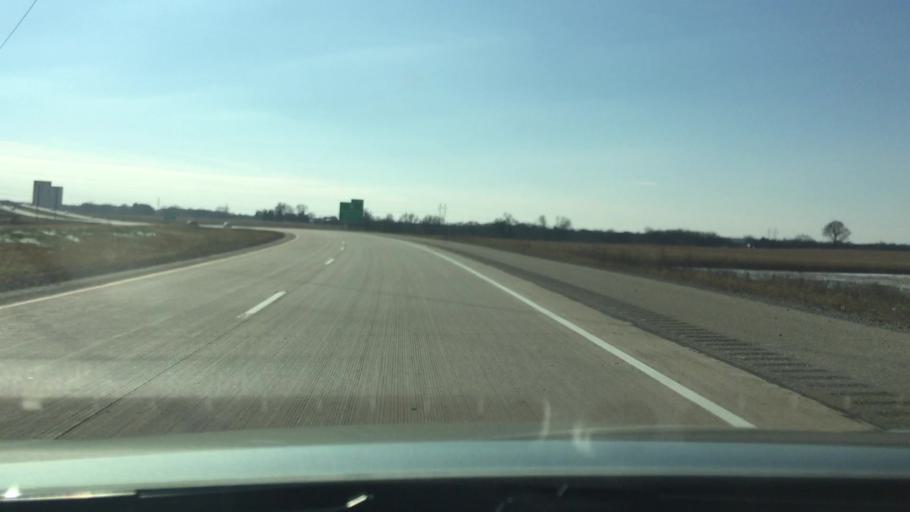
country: US
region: Wisconsin
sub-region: Jefferson County
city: Jefferson
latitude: 43.0257
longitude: -88.8270
